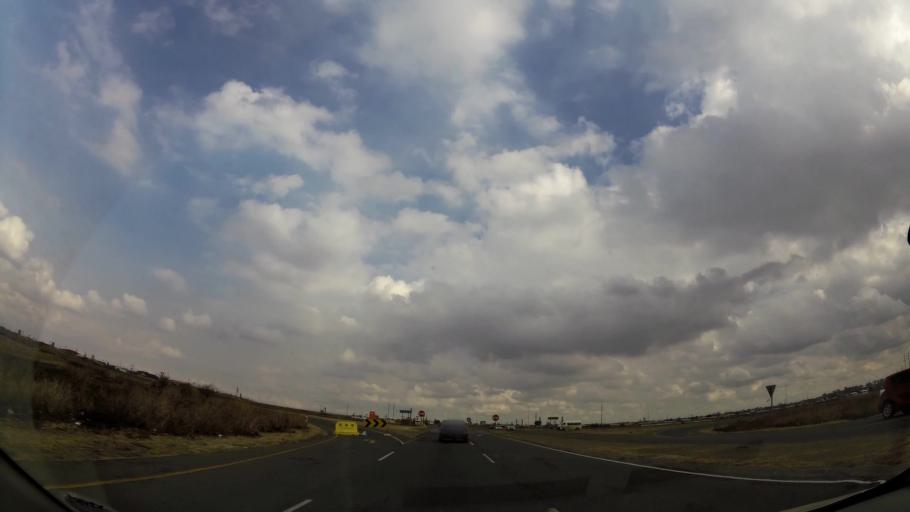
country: ZA
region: Orange Free State
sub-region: Fezile Dabi District Municipality
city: Sasolburg
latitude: -26.8459
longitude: 27.8900
